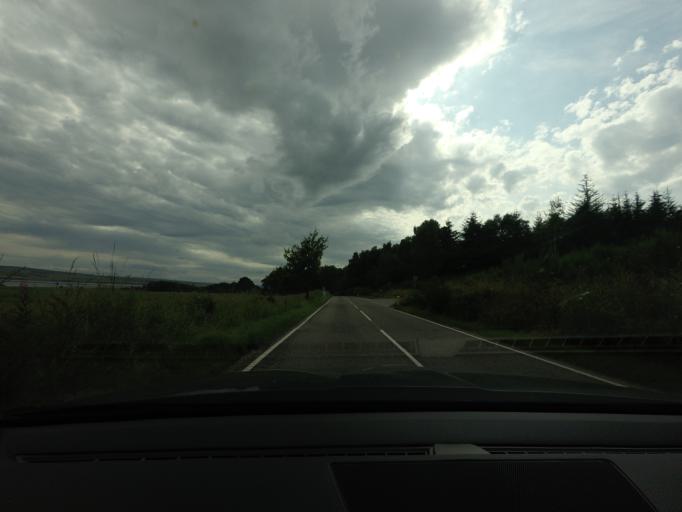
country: GB
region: Scotland
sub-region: Highland
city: Alness
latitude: 57.6948
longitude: -4.2918
